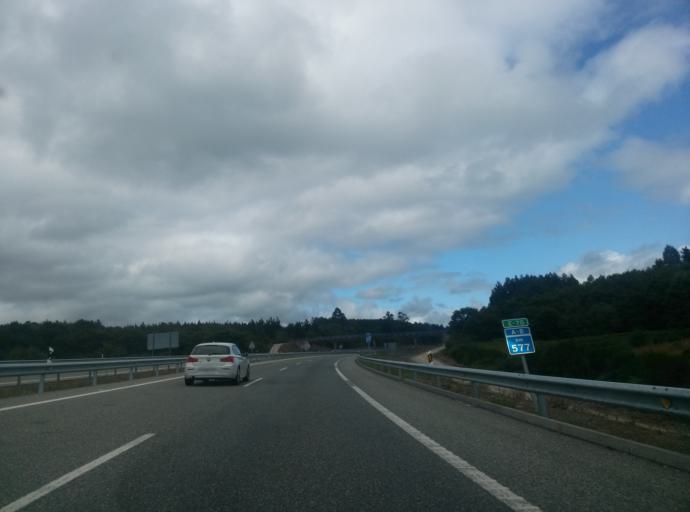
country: ES
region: Galicia
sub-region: Provincia de Lugo
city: Vilalba
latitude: 43.3132
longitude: -7.7052
